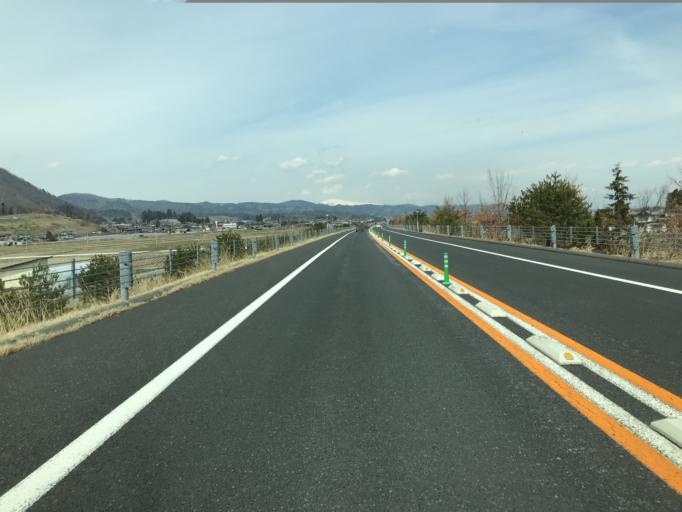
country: JP
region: Yamagata
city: Kaminoyama
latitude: 38.2242
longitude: 140.2796
